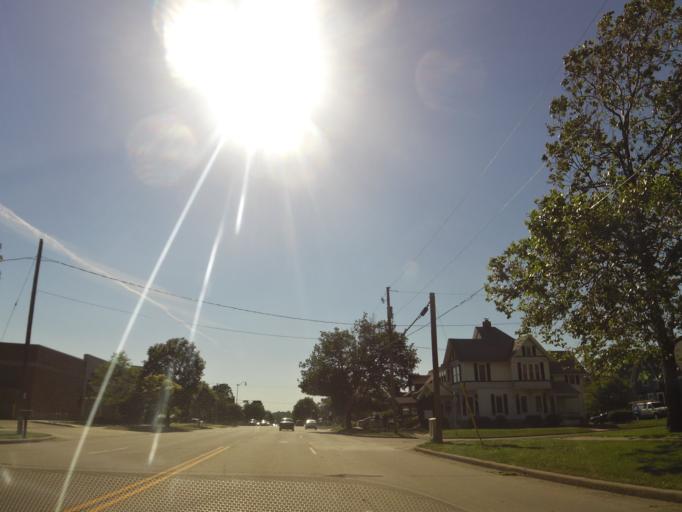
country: US
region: Wisconsin
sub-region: Rock County
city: Beloit
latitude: 42.4987
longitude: -89.0249
